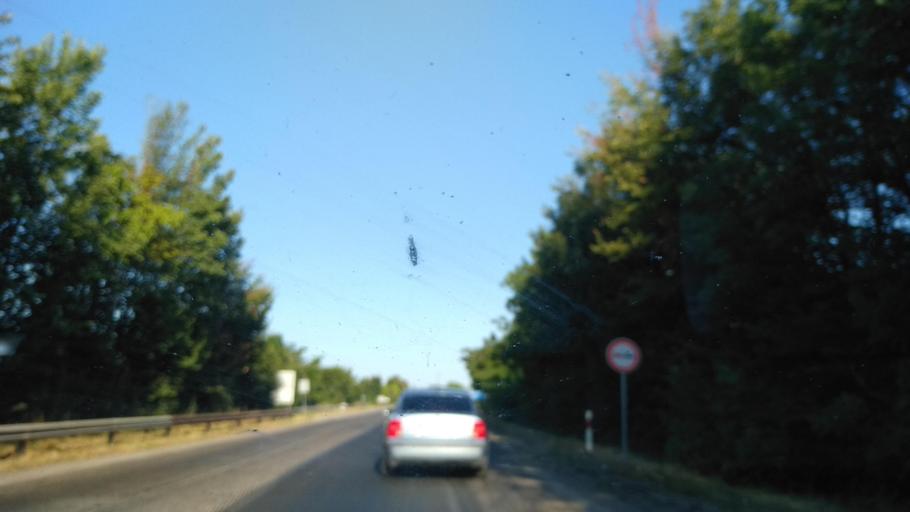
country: BG
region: Gabrovo
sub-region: Obshtina Dryanovo
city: Dryanovo
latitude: 43.0881
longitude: 25.4653
